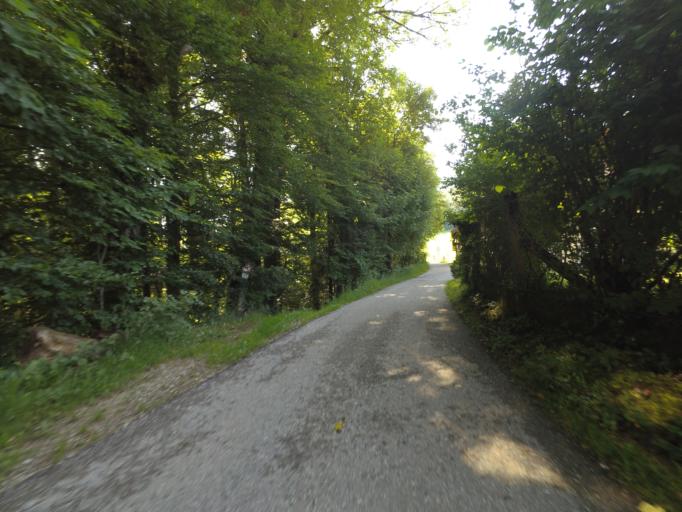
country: DE
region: Bavaria
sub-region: Upper Bavaria
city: Piding
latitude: 47.7376
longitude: 12.9365
